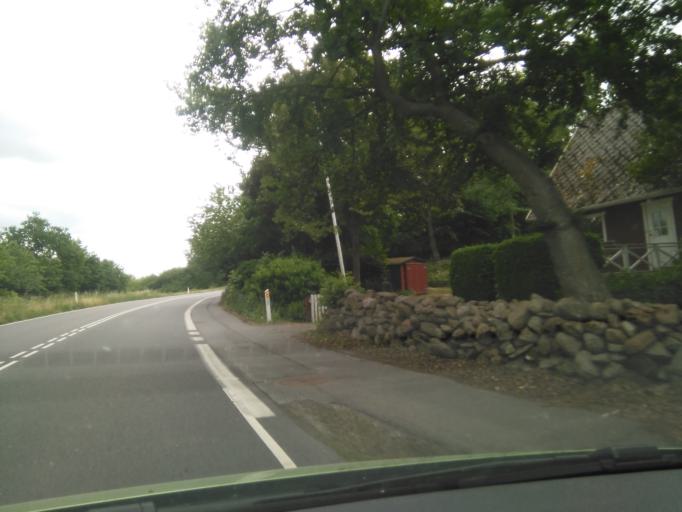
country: DK
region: Capital Region
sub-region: Bornholm Kommune
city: Akirkeby
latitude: 55.2369
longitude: 14.8736
